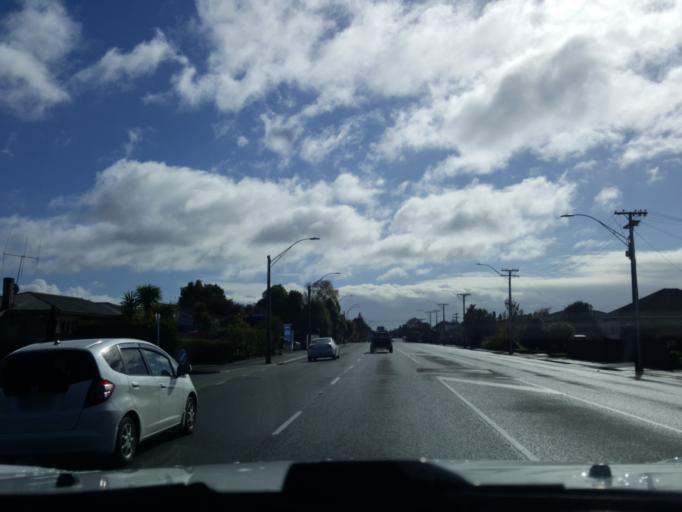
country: NZ
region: Waikato
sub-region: Hamilton City
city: Hamilton
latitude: -37.7739
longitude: 175.2642
